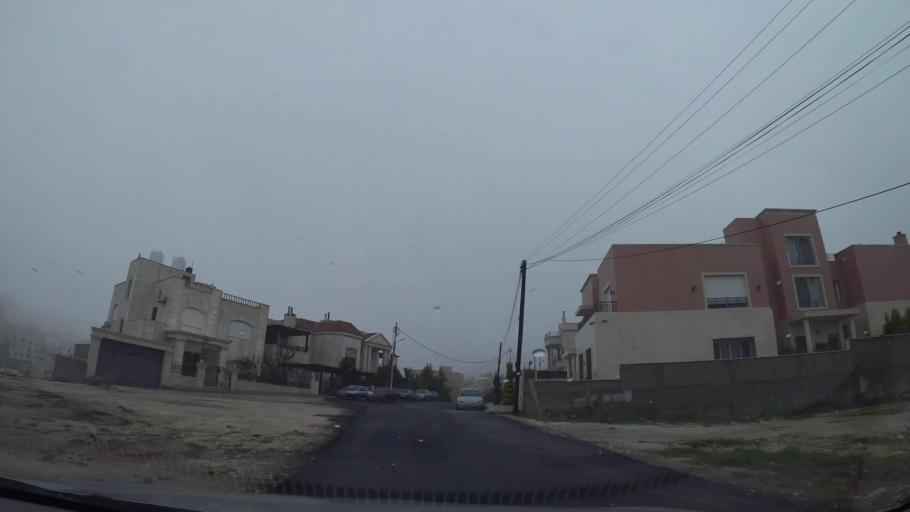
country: JO
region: Amman
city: Al Jubayhah
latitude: 32.0118
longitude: 35.8346
